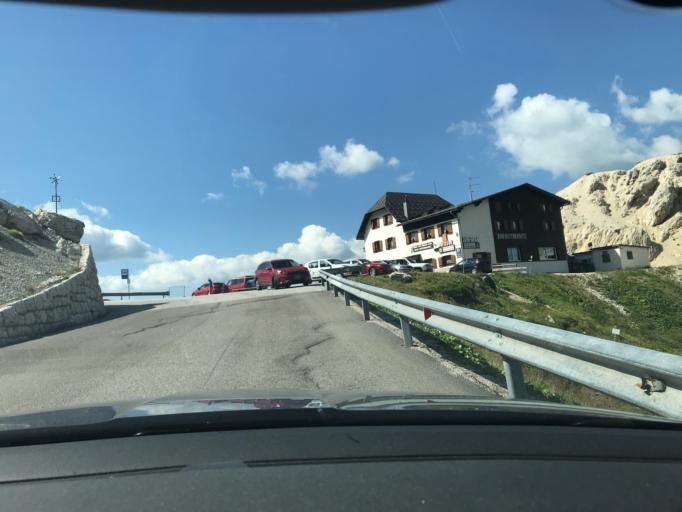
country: IT
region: Veneto
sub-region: Provincia di Belluno
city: Livinallongo del Col di Lana
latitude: 46.5322
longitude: 11.9890
